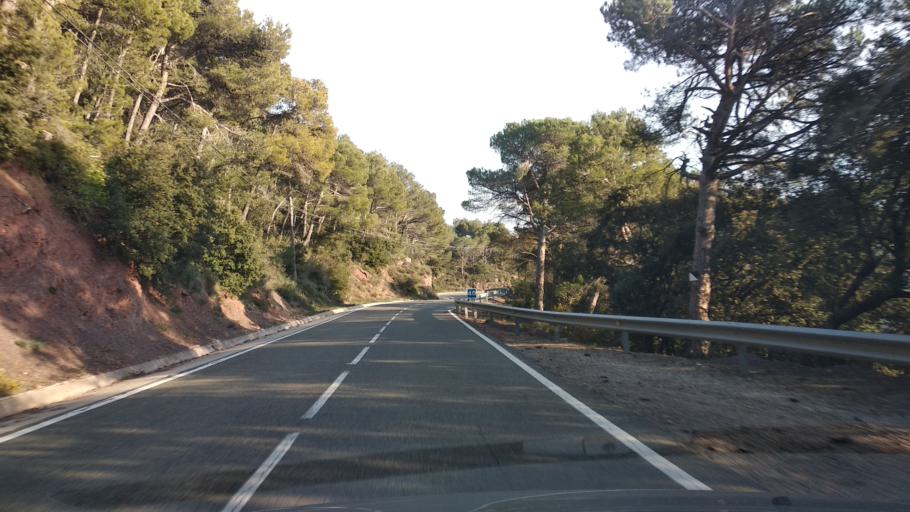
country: ES
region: Catalonia
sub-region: Provincia de Tarragona
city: Alforja
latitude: 41.2210
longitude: 0.9448
